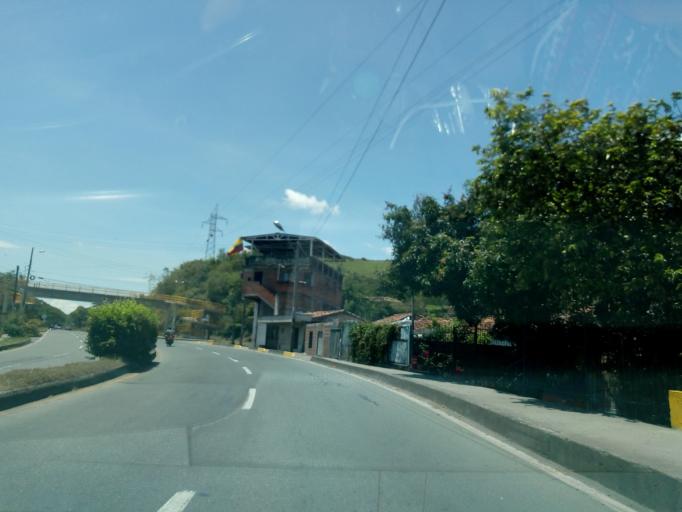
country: CO
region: Valle del Cauca
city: Cartago
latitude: 4.7329
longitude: -75.9045
